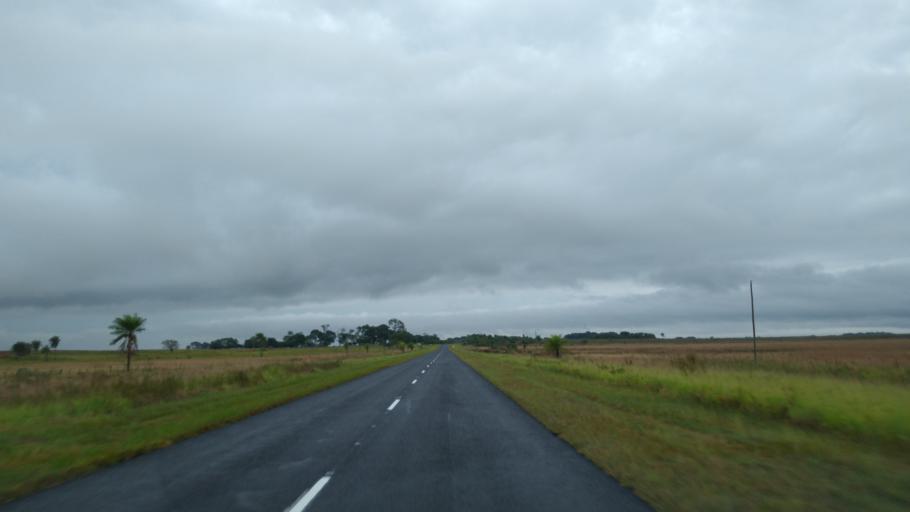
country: AR
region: Corrientes
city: Loreto
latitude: -27.7145
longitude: -57.2292
